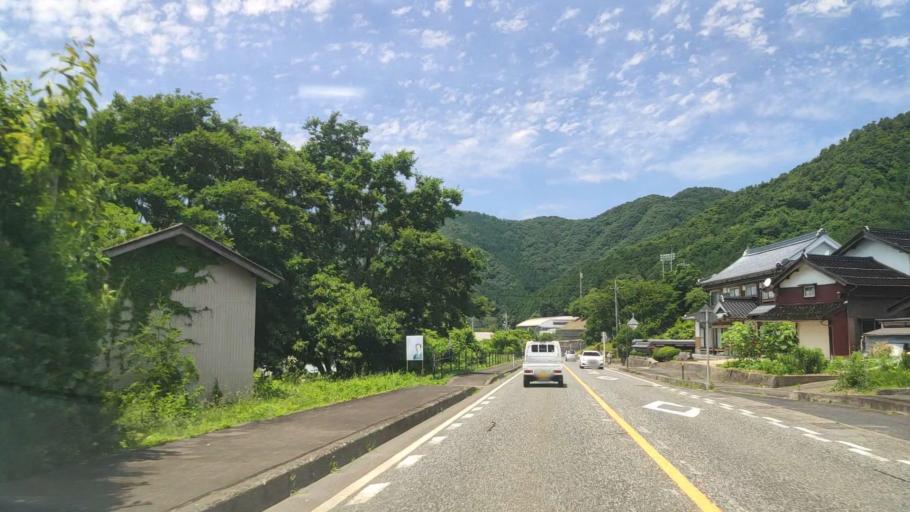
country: JP
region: Tottori
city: Tottori
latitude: 35.3639
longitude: 134.3436
